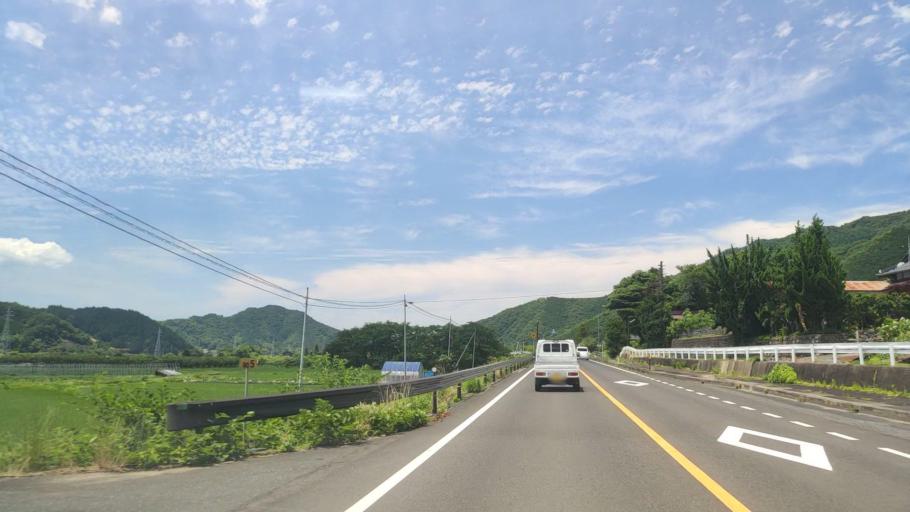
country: JP
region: Tottori
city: Tottori
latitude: 35.3688
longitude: 134.3116
